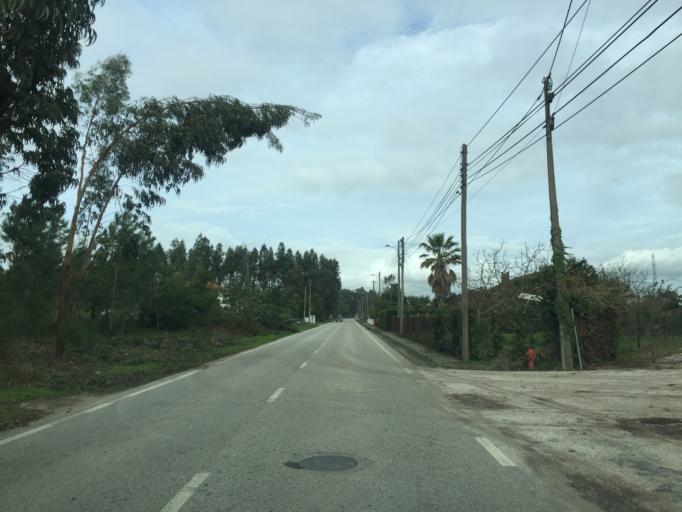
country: PT
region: Coimbra
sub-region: Figueira da Foz
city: Lavos
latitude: 40.0413
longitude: -8.8189
